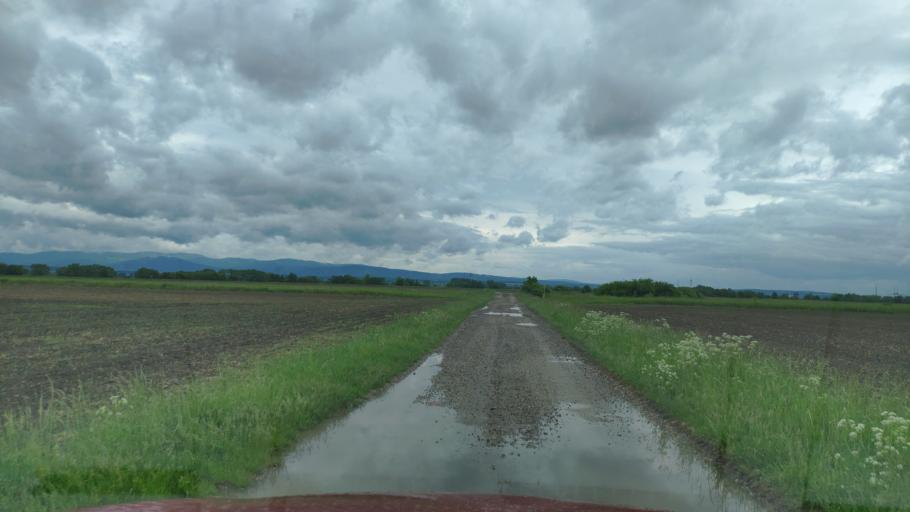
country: SK
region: Kosicky
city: Moldava nad Bodvou
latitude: 48.5502
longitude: 21.1135
